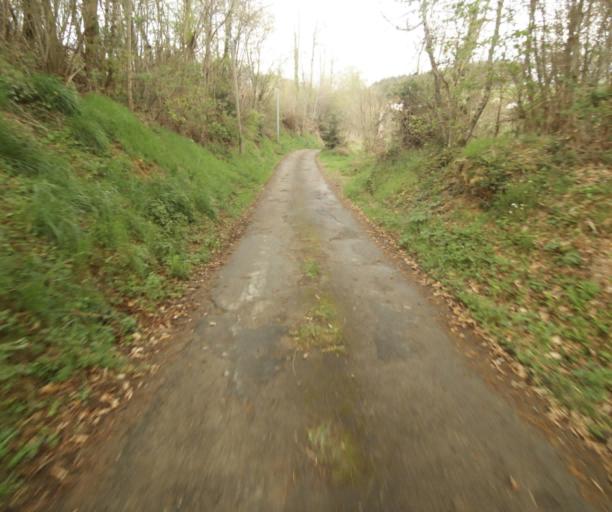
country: FR
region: Limousin
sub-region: Departement de la Correze
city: Tulle
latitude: 45.2815
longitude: 1.7482
